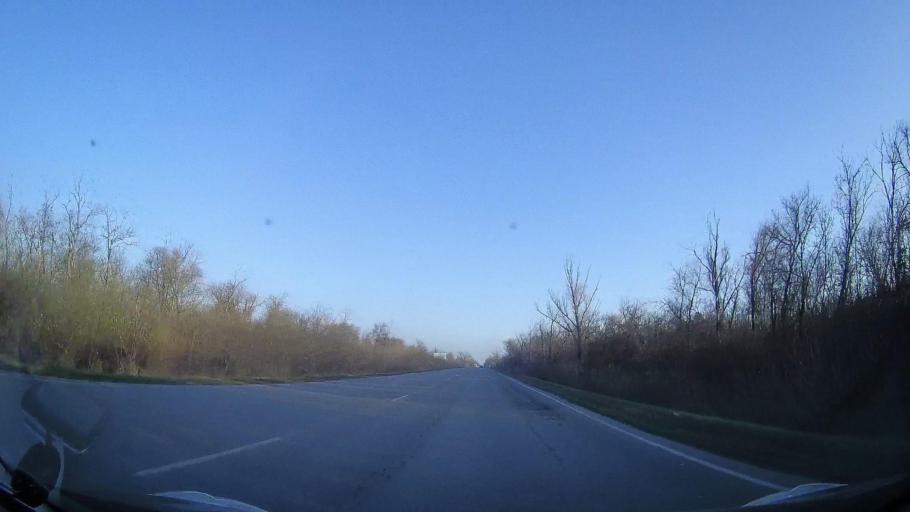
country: RU
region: Rostov
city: Bataysk
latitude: 47.0532
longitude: 39.8320
